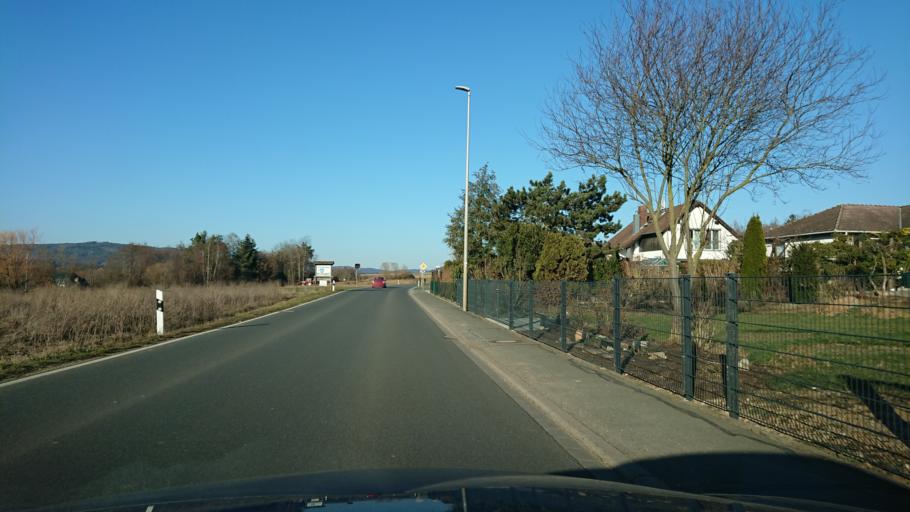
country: DE
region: Bavaria
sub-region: Upper Franconia
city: Kirchehrenbach
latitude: 49.7381
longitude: 11.1534
